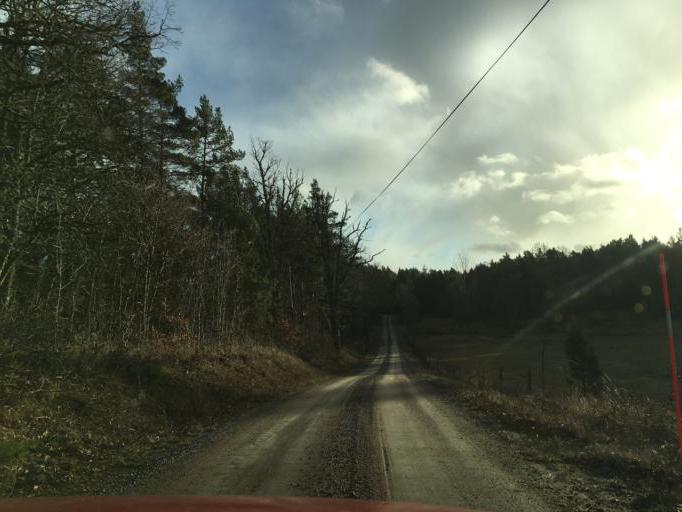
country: SE
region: Kalmar
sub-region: Vasterviks Kommun
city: Vaestervik
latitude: 57.6230
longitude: 16.5374
